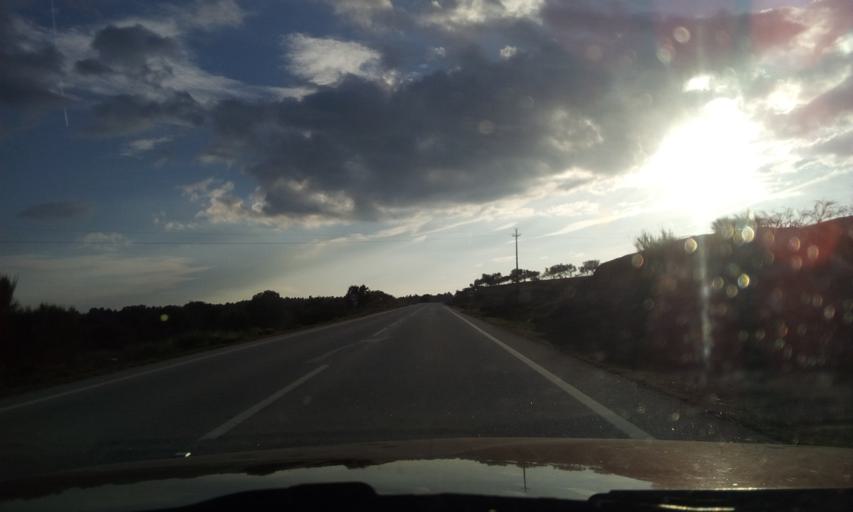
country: PT
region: Guarda
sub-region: Pinhel
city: Pinhel
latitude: 40.6660
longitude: -6.9596
